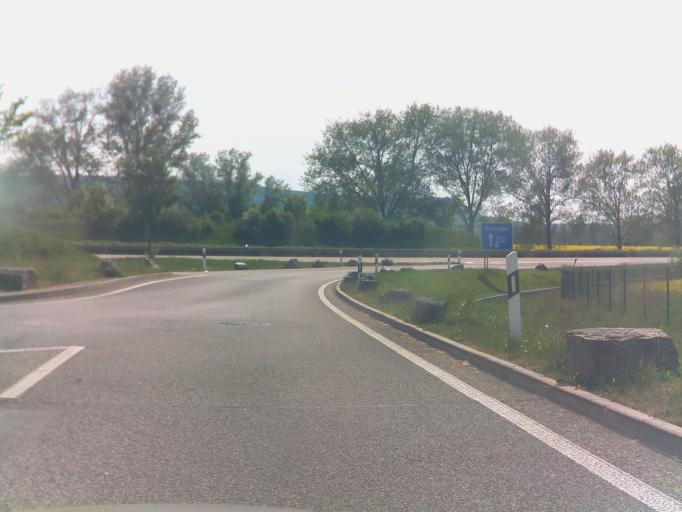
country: DE
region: Thuringia
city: Niedergebra
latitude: 51.4350
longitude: 10.6229
